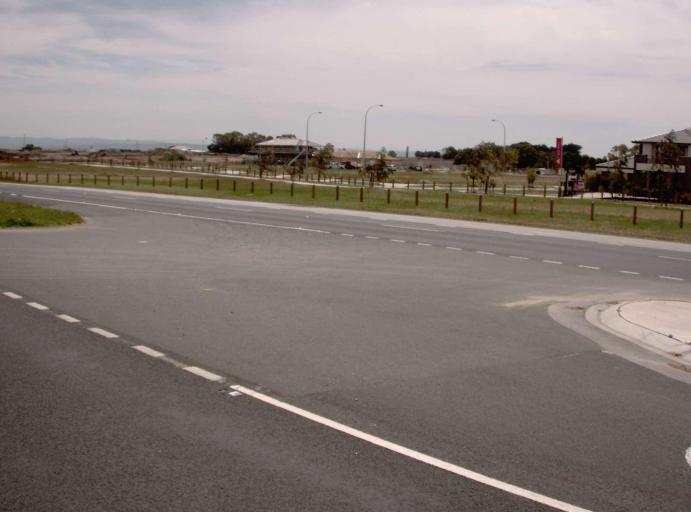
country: AU
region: Victoria
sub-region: Frankston
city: Skye
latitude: -38.1128
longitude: 145.2323
